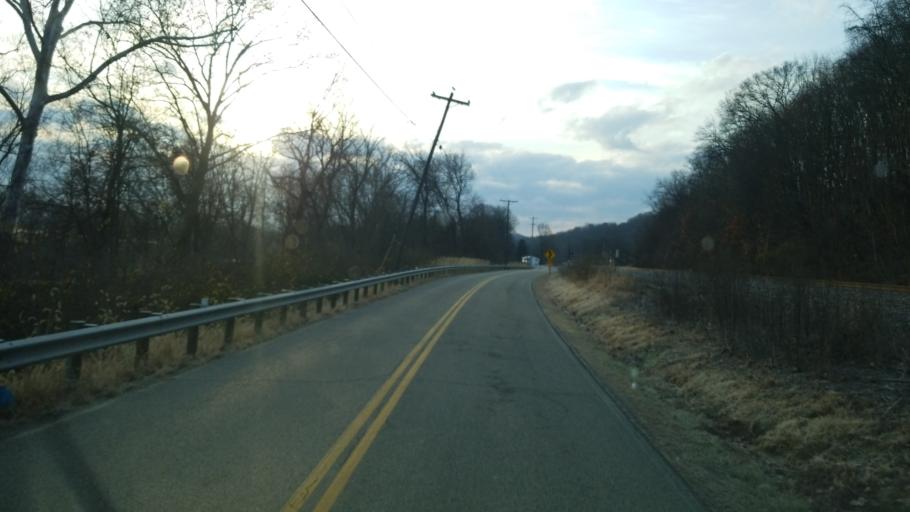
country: US
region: Ohio
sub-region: Ross County
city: Chillicothe
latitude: 39.2745
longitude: -82.9287
